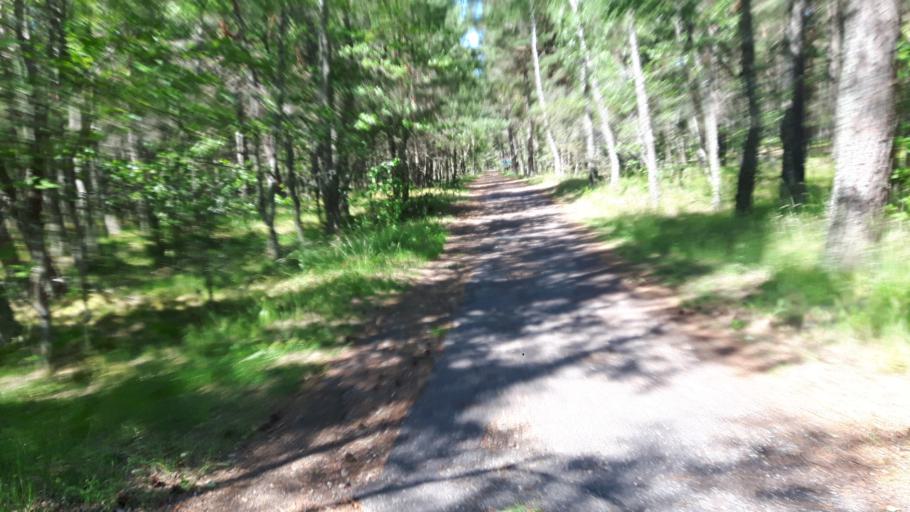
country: LT
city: Neringa
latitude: 55.4157
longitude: 21.0812
